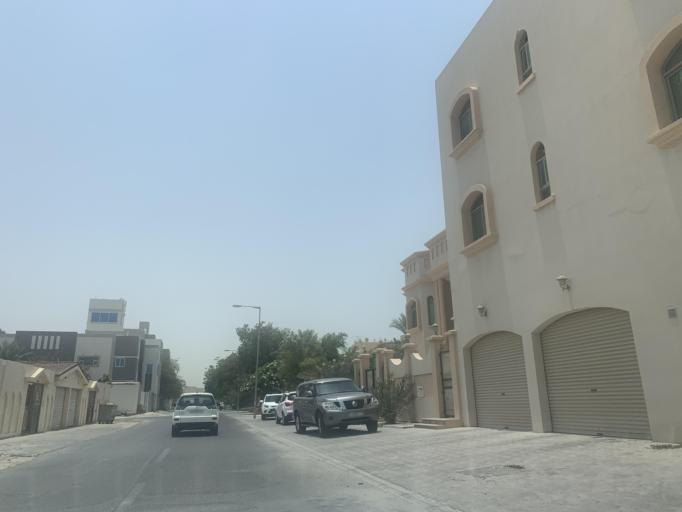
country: BH
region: Manama
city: Jidd Hafs
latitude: 26.2224
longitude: 50.4590
